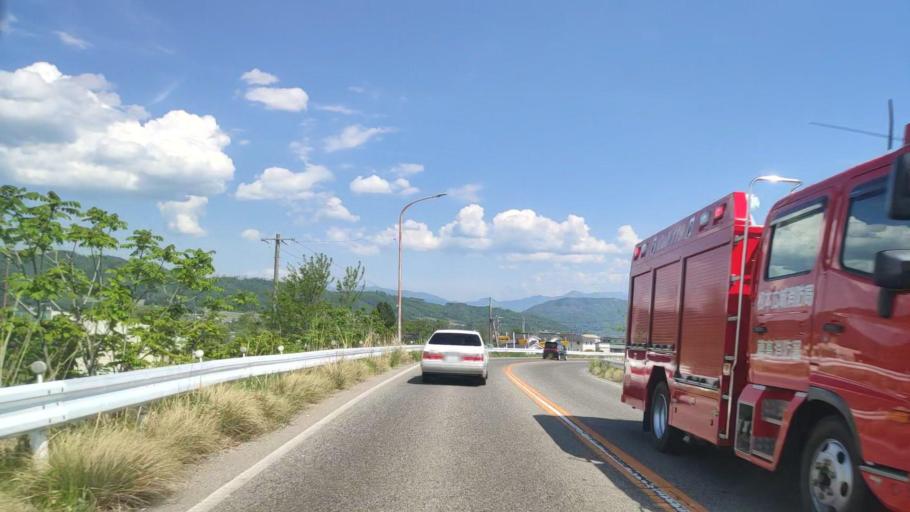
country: JP
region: Nagano
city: Hotaka
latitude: 36.3770
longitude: 137.8710
